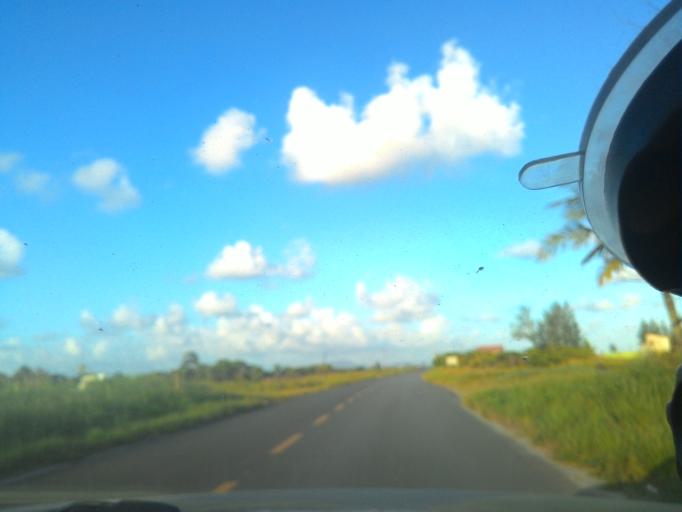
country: BR
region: Sao Paulo
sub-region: Iguape
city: Iguape
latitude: -24.8249
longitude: -47.6633
